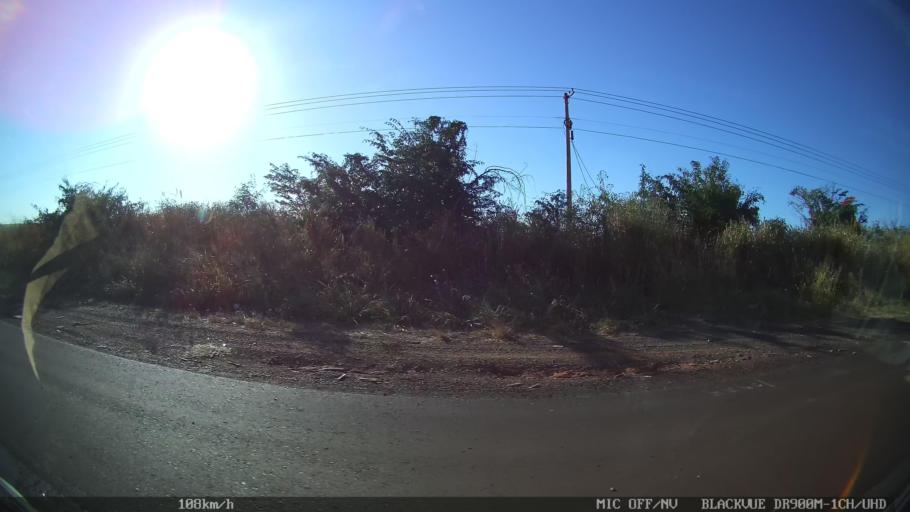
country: BR
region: Sao Paulo
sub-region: Olimpia
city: Olimpia
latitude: -20.7269
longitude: -49.0407
